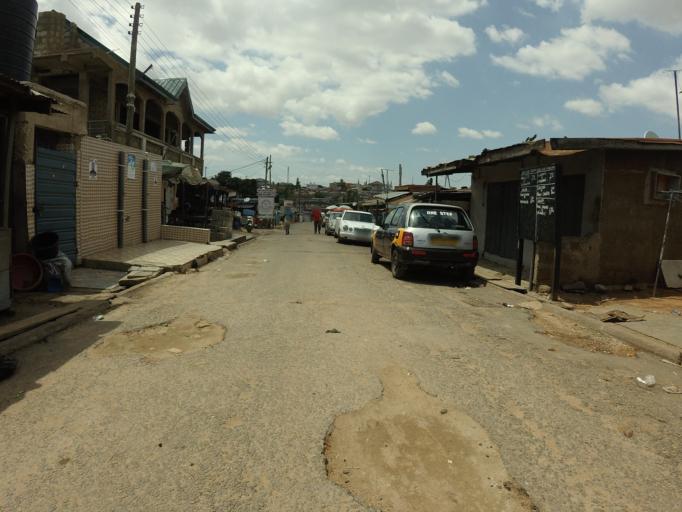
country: GH
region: Greater Accra
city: Accra
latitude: 5.5816
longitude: -0.2023
